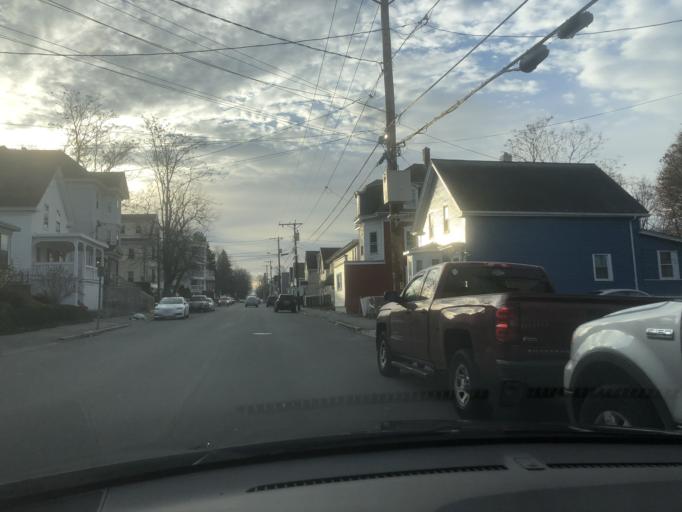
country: US
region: Massachusetts
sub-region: Essex County
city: Lawrence
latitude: 42.7156
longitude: -71.1535
